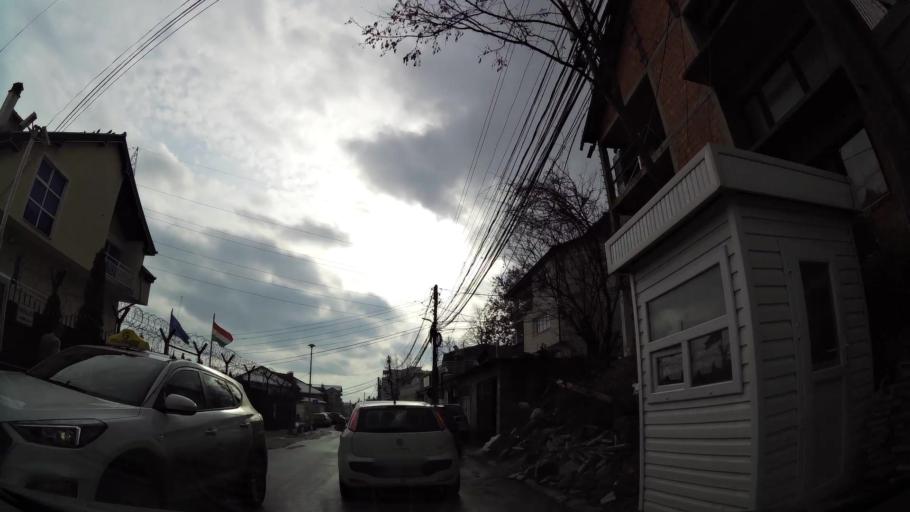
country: XK
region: Pristina
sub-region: Komuna e Prishtines
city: Pristina
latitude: 42.6655
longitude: 21.1523
